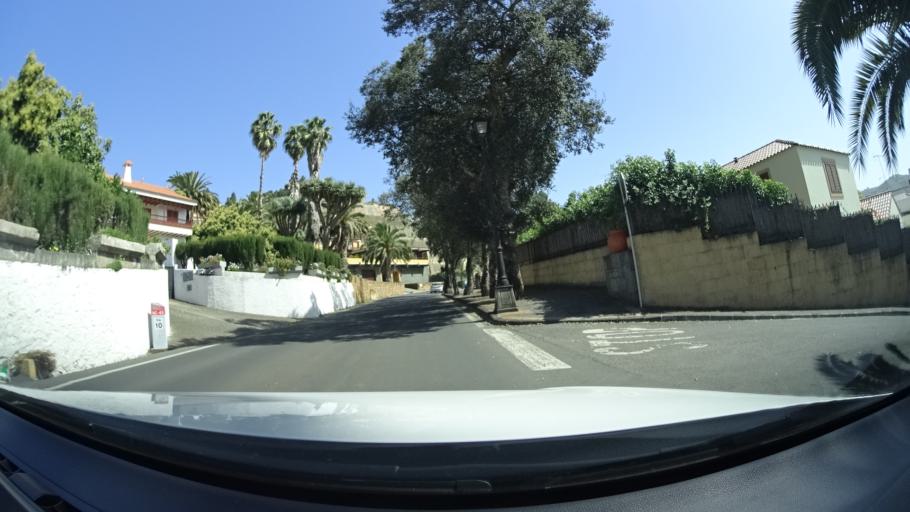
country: ES
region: Canary Islands
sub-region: Provincia de Las Palmas
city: Teror
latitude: 28.0652
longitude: -15.5438
